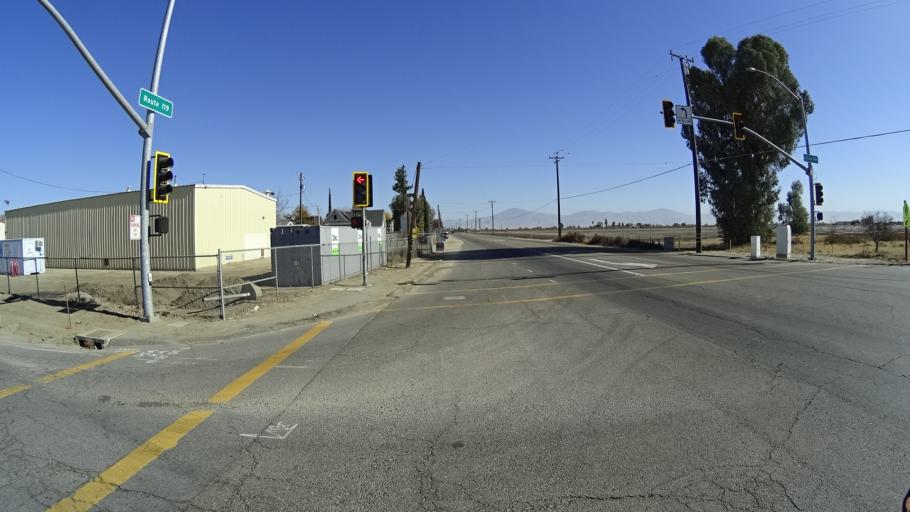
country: US
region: California
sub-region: Kern County
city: Greenfield
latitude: 35.2671
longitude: -119.0567
